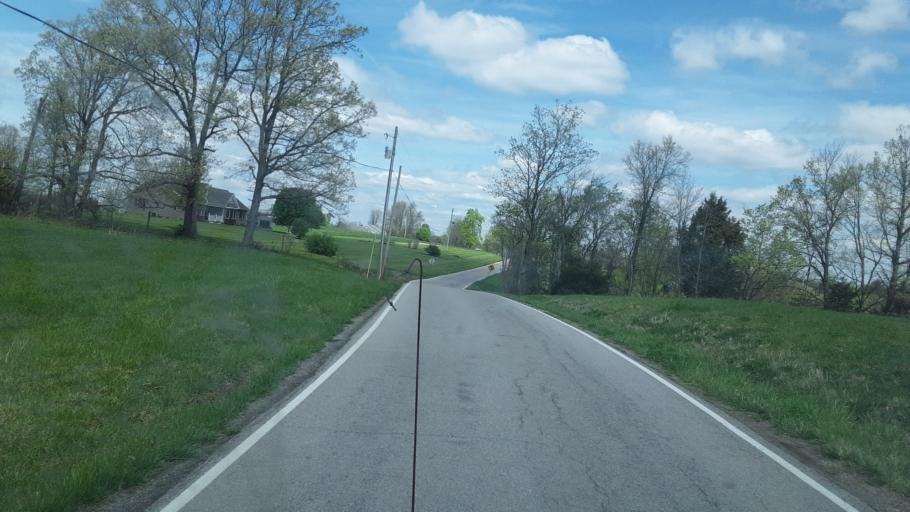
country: US
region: Kentucky
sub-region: Owen County
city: Owenton
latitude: 38.6484
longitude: -84.7724
